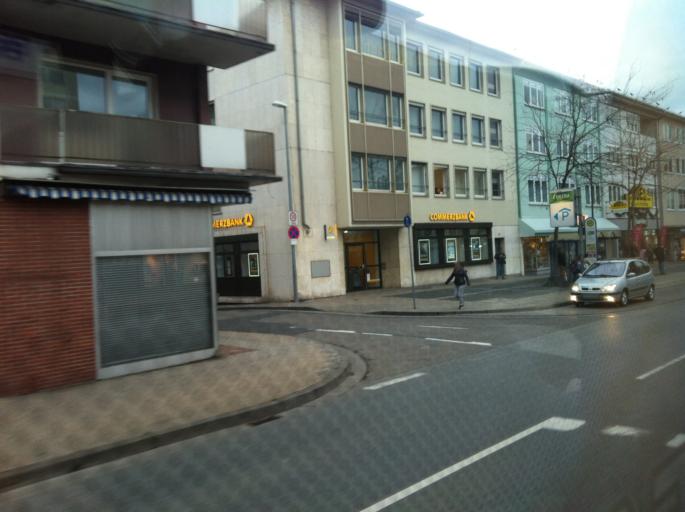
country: DE
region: Rheinland-Pfalz
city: Bad Kreuznach
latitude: 49.8380
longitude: 7.8550
